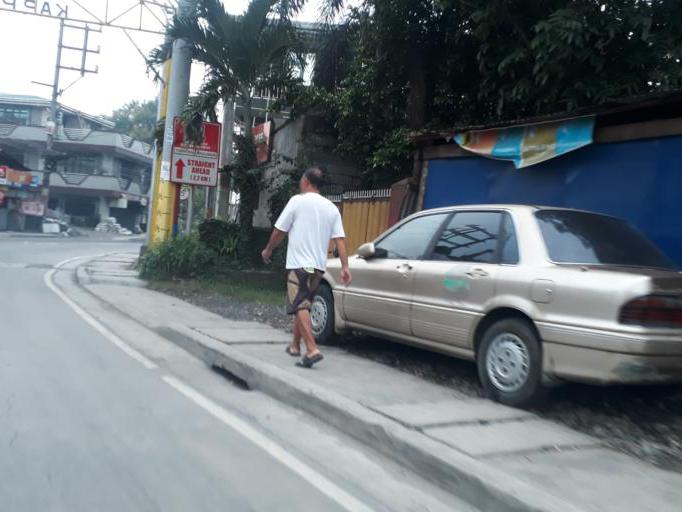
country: PH
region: Metro Manila
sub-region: Caloocan City
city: Niugan
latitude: 14.6749
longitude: 120.9633
